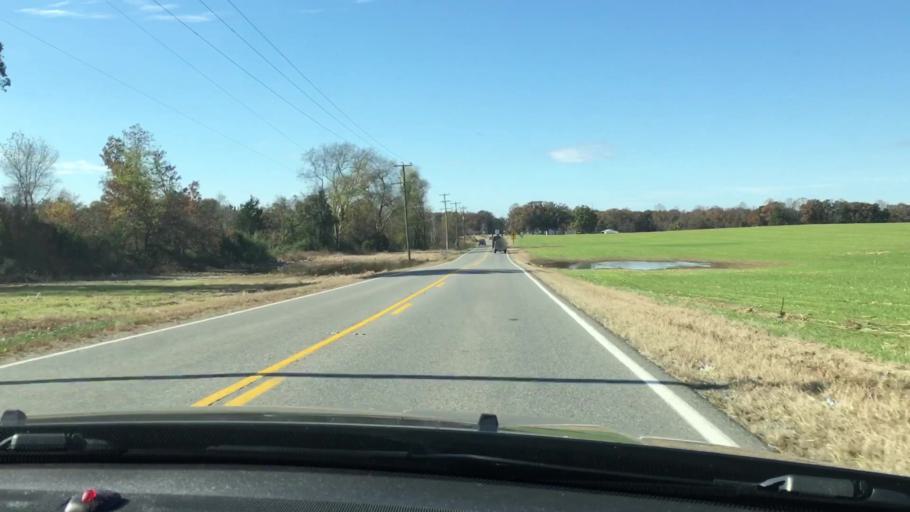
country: US
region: Virginia
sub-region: King William County
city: Central Garage
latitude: 37.7273
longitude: -77.0970
